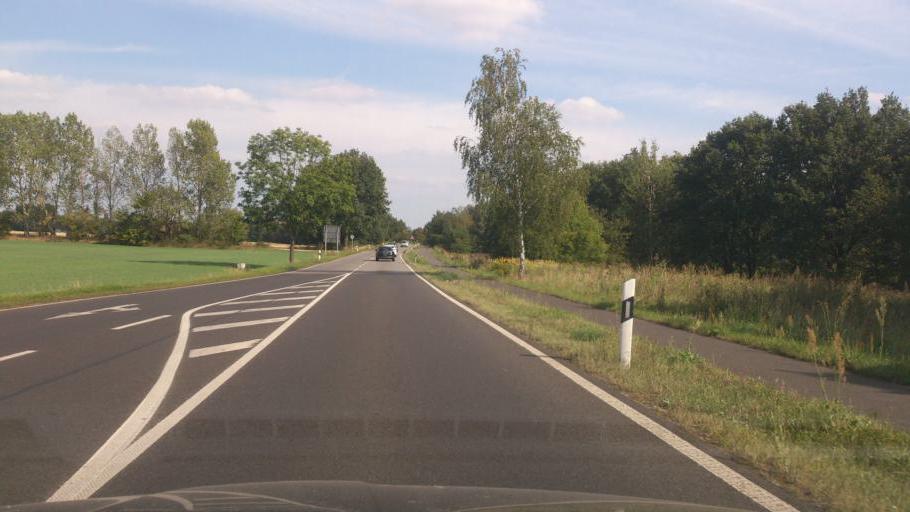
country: DE
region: Brandenburg
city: Ludwigsfelde
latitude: 52.3185
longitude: 13.2156
